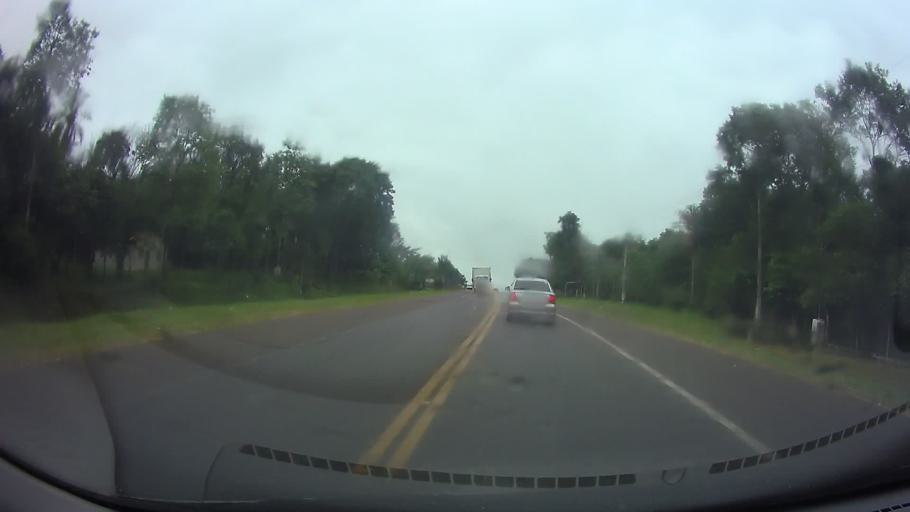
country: PY
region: Central
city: Ita
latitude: -25.5321
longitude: -57.3317
